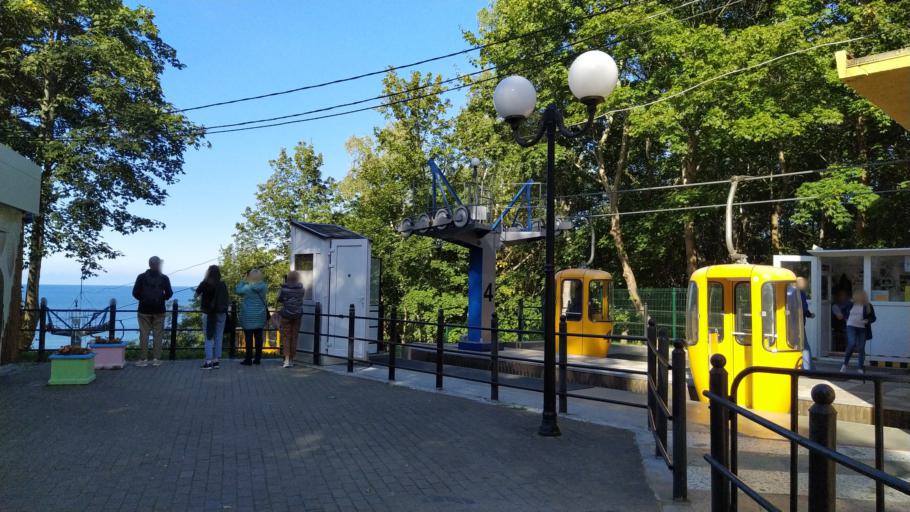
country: RU
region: Kaliningrad
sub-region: Gorod Svetlogorsk
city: Svetlogorsk
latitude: 54.9446
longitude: 20.1466
